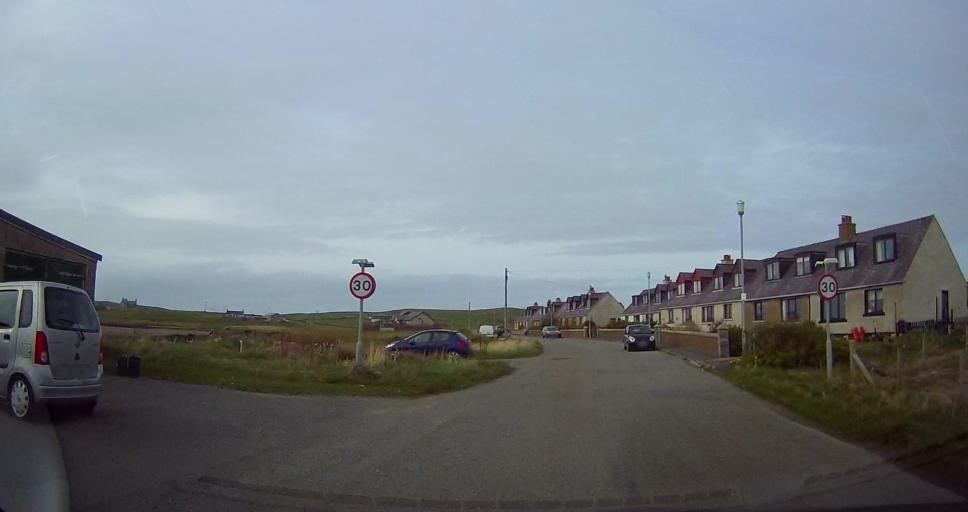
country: GB
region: Scotland
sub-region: Shetland Islands
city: Shetland
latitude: 60.1537
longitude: -1.1159
